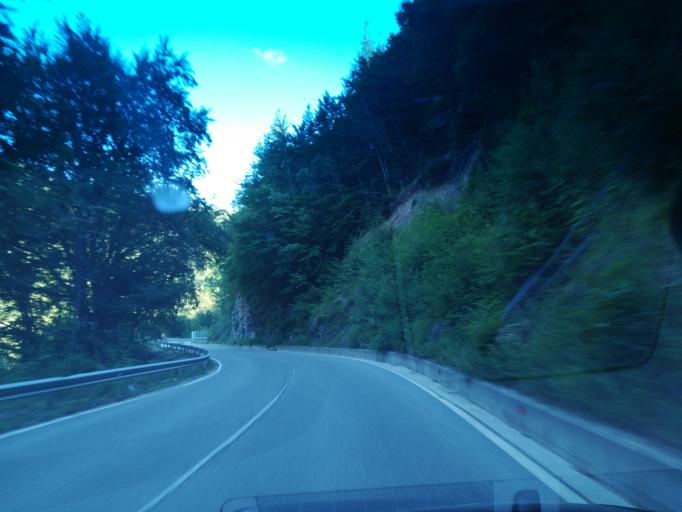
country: BG
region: Smolyan
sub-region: Obshtina Chepelare
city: Chepelare
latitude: 41.8106
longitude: 24.7056
